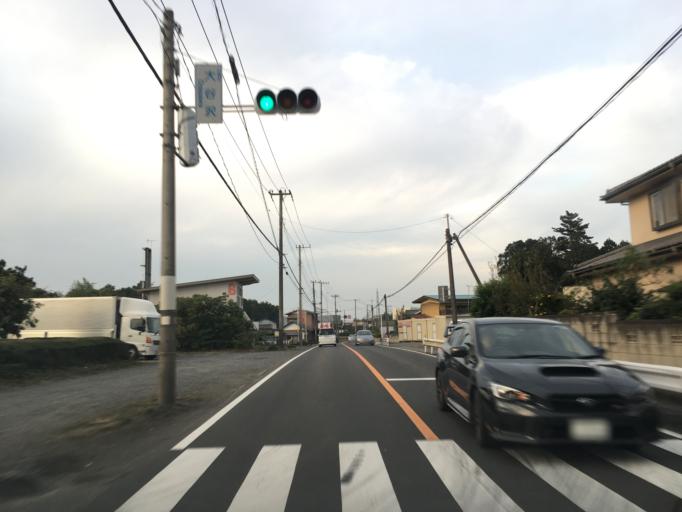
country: JP
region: Saitama
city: Sayama
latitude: 35.8830
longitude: 139.3772
